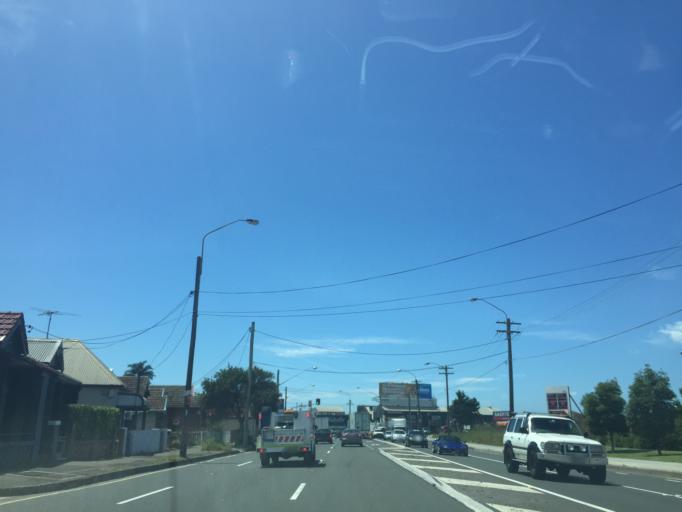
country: AU
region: New South Wales
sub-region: Marrickville
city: Marrickville
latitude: -33.9209
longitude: 151.1665
